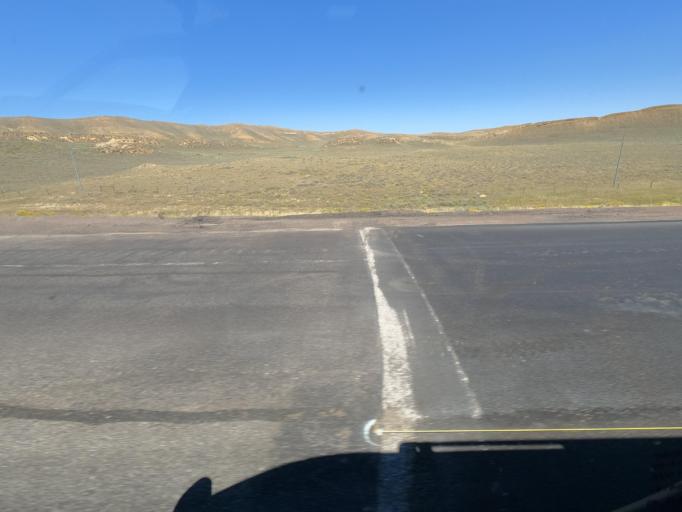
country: US
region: Wyoming
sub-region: Carbon County
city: Saratoga
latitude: 41.7502
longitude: -106.5040
